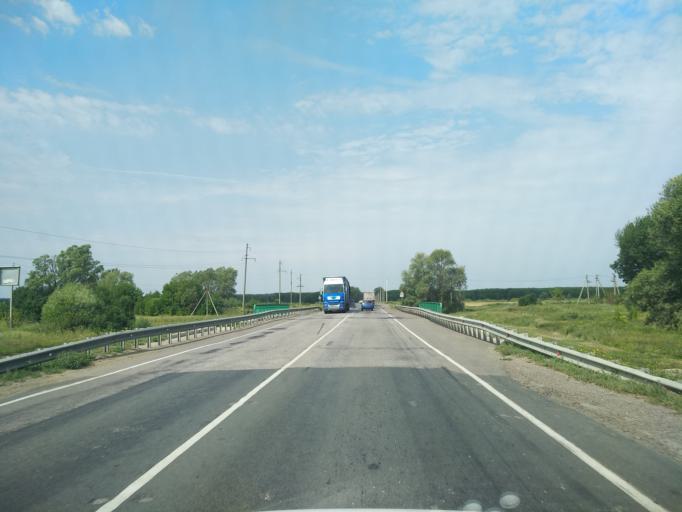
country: RU
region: Voronezj
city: Orlovo
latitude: 51.6803
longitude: 39.6109
